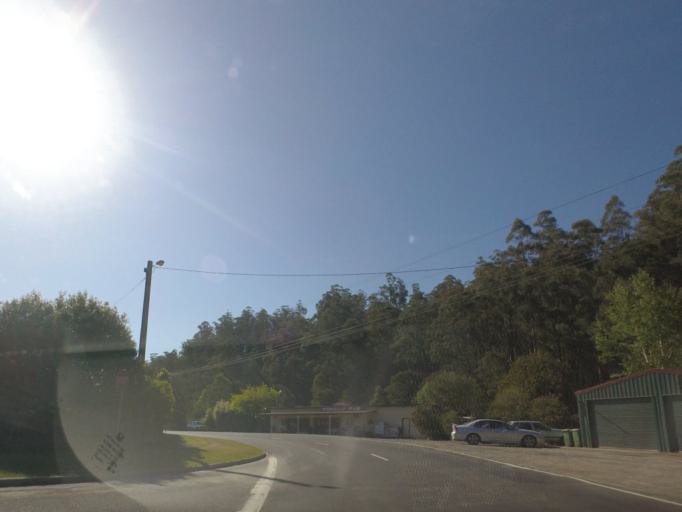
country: AU
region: Victoria
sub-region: Yarra Ranges
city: Millgrove
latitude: -37.8635
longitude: 145.7534
